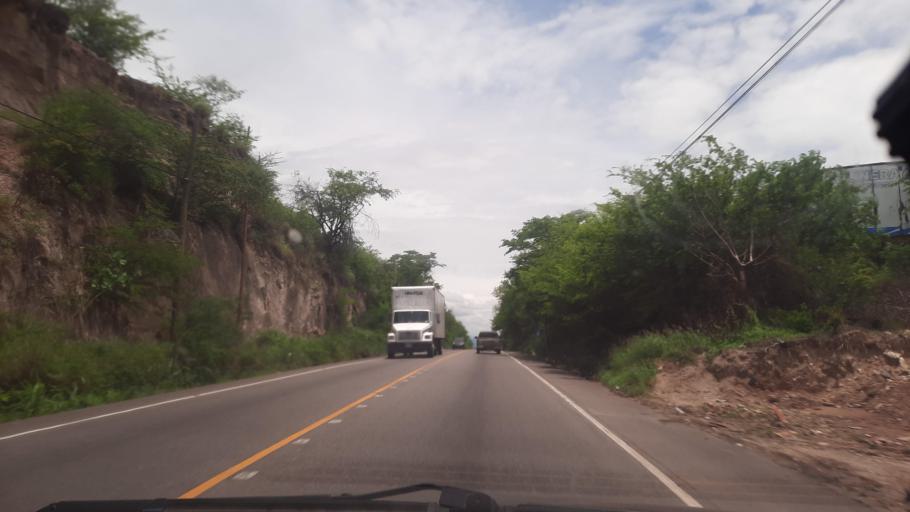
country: GT
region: Zacapa
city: Rio Hondo
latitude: 15.0450
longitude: -89.5735
